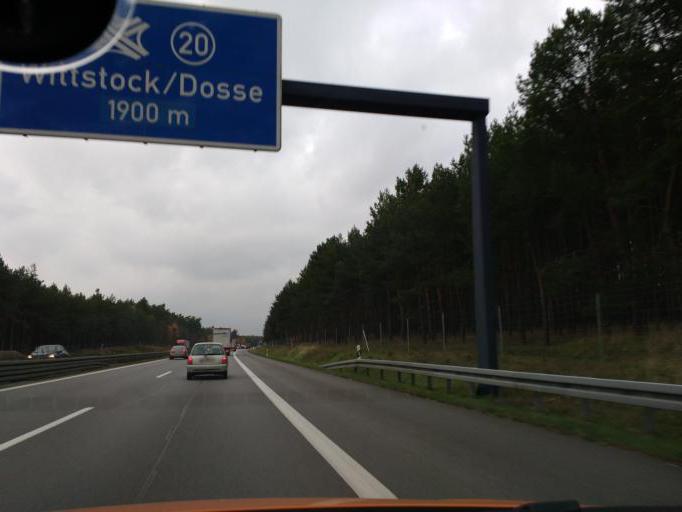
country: DE
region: Brandenburg
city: Wittstock
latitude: 53.1066
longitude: 12.4797
